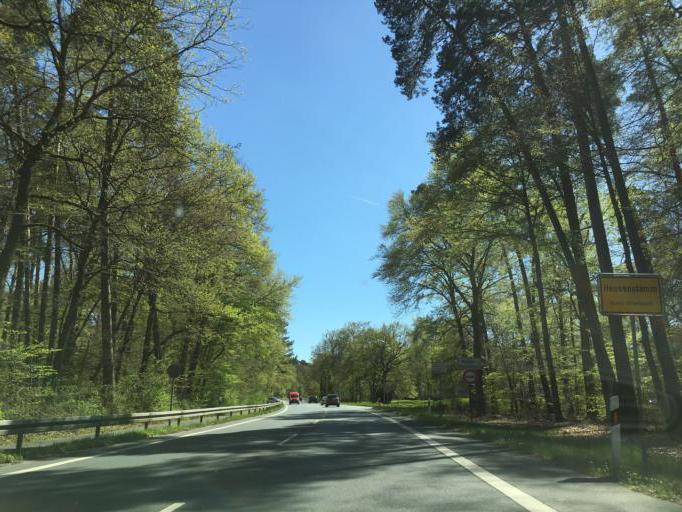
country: DE
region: Hesse
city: Heusenstamm
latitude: 50.0628
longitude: 8.7900
